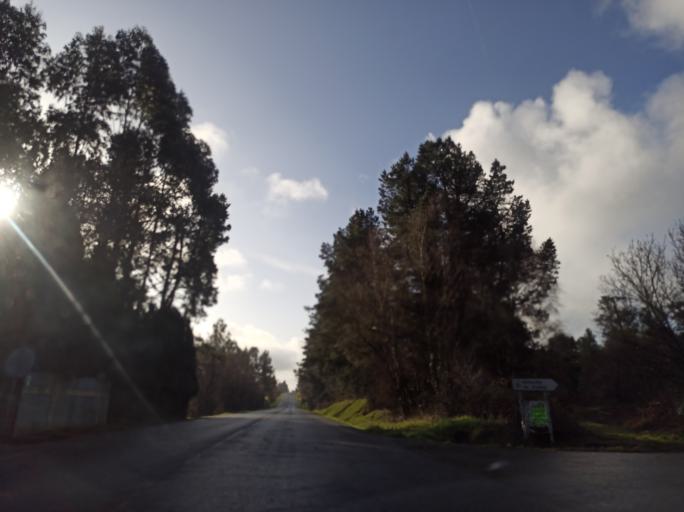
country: ES
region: Galicia
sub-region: Provincia da Coruna
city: Curtis
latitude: 43.1266
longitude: -8.0315
